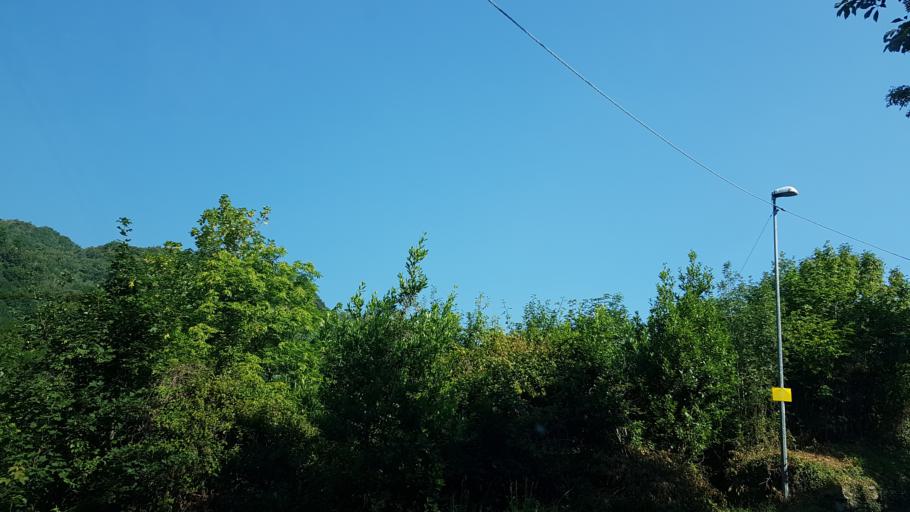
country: IT
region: Liguria
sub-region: Provincia di Genova
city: Serra Ricco
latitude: 44.5200
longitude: 8.9411
